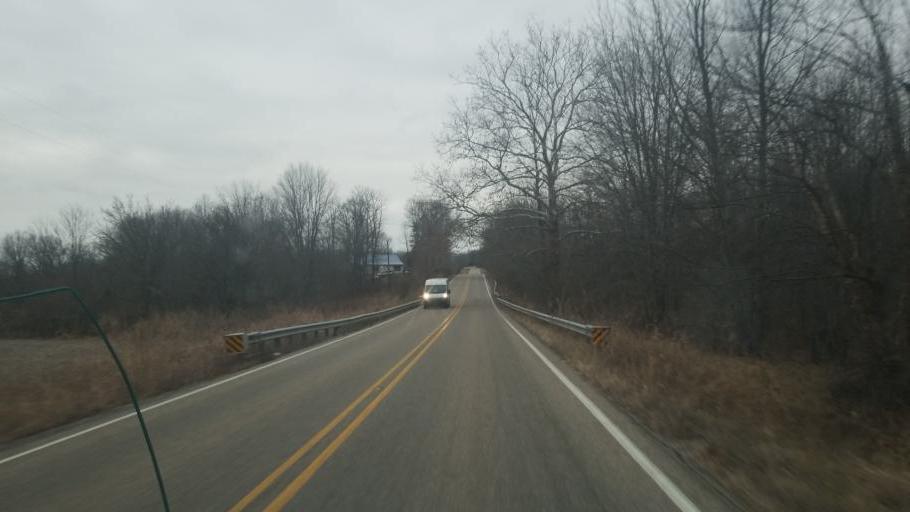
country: US
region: Indiana
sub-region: Owen County
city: Spencer
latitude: 39.3525
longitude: -86.9303
